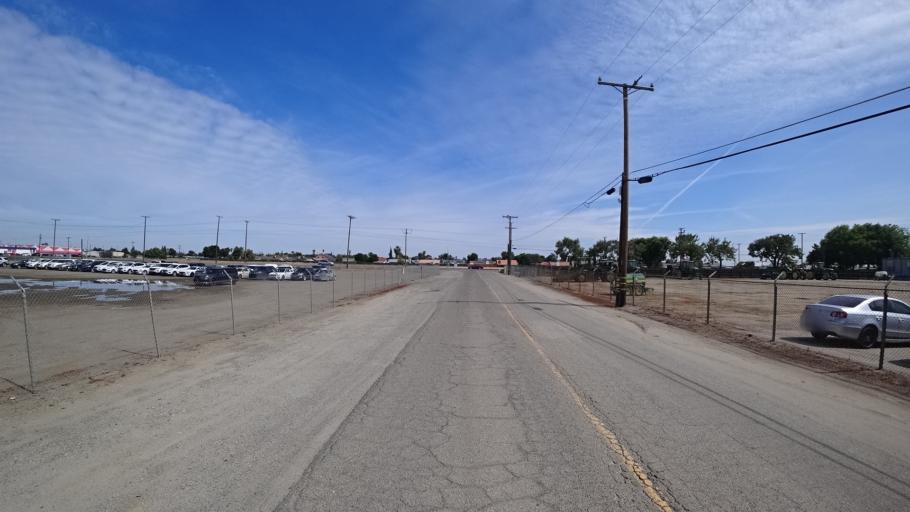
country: US
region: California
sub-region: Kings County
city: Hanford
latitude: 36.3272
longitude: -119.6258
